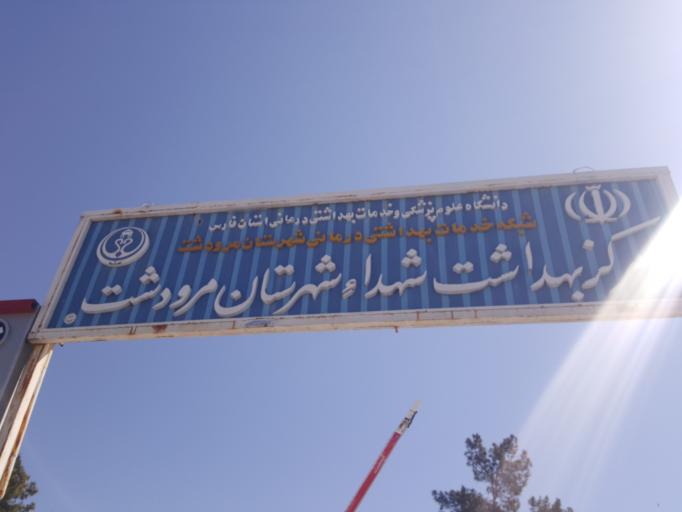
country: IR
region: Fars
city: Marvdasht
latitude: 29.8793
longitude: 52.8215
